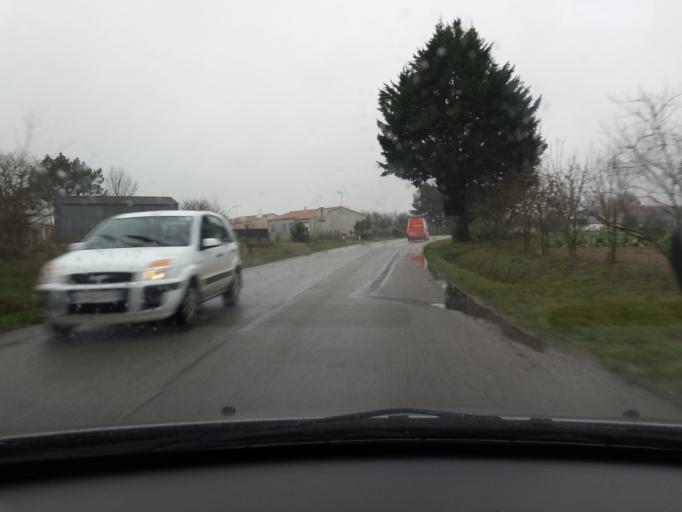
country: FR
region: Pays de la Loire
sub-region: Departement de la Vendee
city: Mareuil-sur-Lay-Dissais
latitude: 46.5520
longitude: -1.1573
